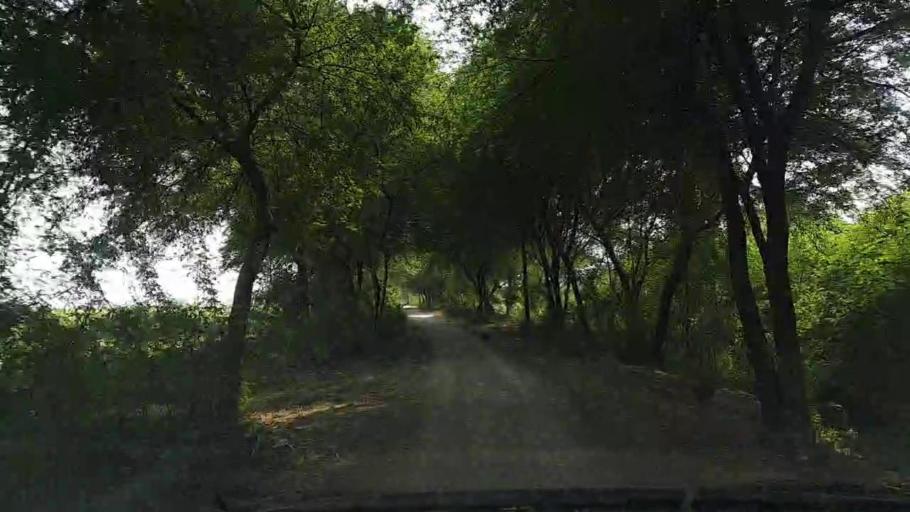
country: PK
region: Sindh
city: Mirpur Batoro
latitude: 24.6903
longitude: 68.2211
